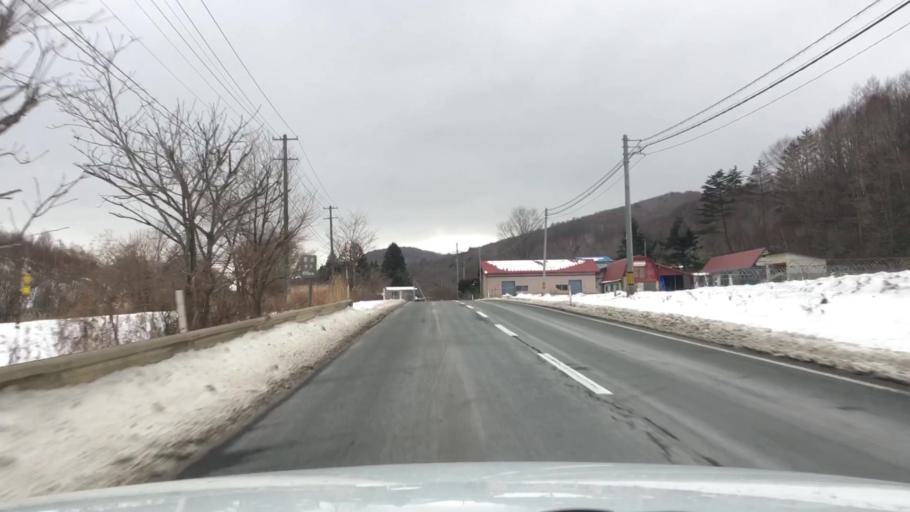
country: JP
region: Iwate
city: Morioka-shi
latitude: 39.6427
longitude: 141.4016
